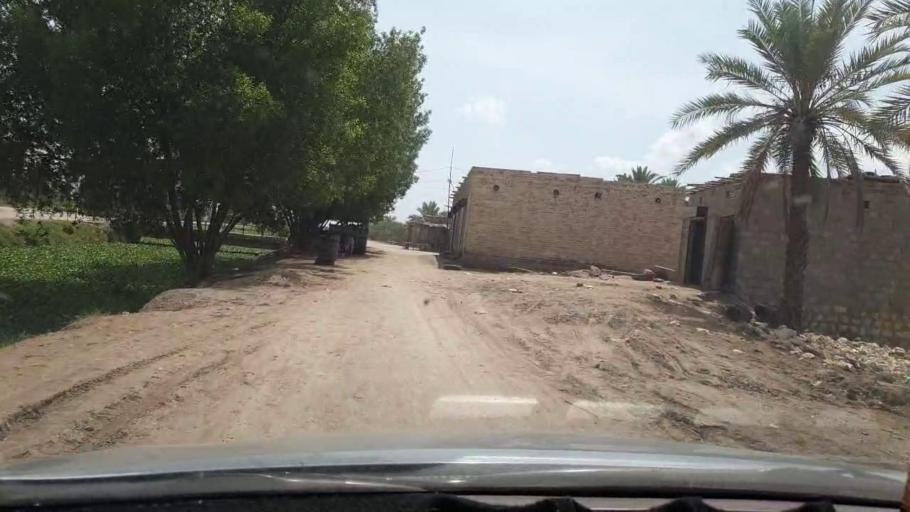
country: PK
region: Sindh
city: Khairpur
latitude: 27.4512
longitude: 68.7871
